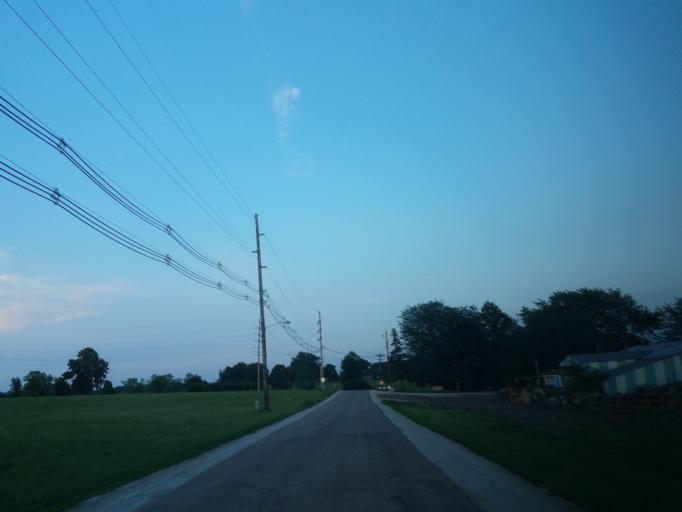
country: US
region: Illinois
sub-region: McLean County
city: Bloomington
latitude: 40.4444
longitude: -89.0071
